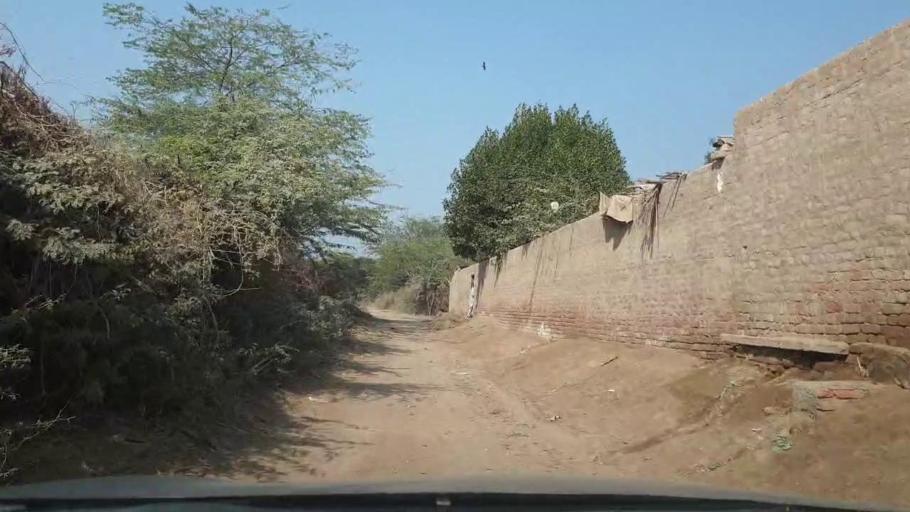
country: PK
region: Sindh
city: Tando Allahyar
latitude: 25.5917
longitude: 68.8281
